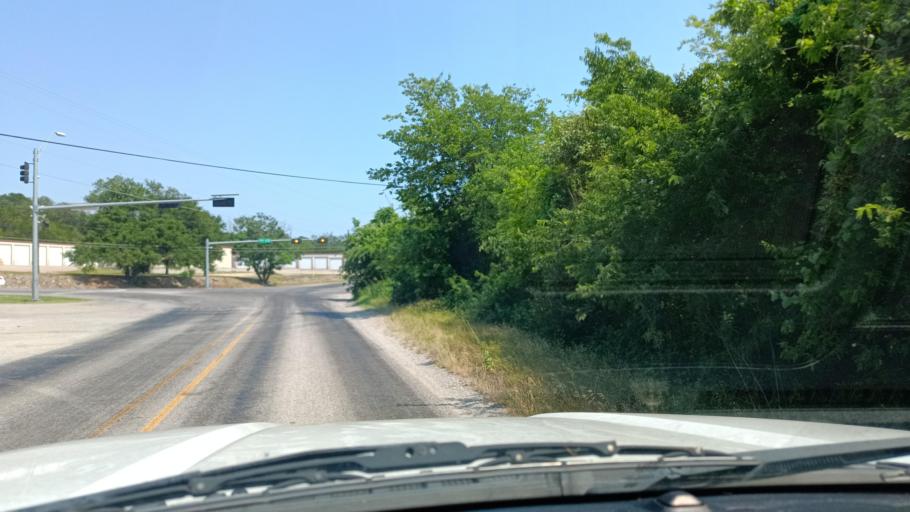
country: US
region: Texas
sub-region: Bell County
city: Belton
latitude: 31.1006
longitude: -97.5171
